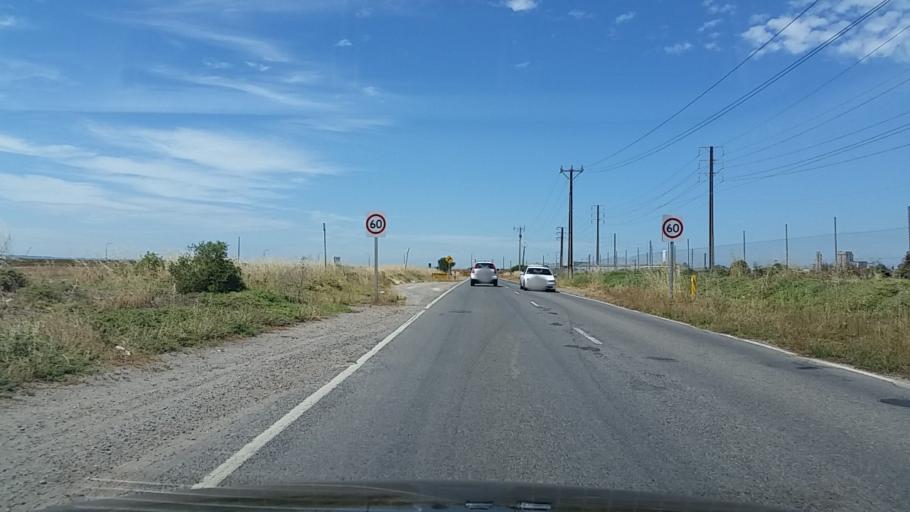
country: AU
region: South Australia
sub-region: Port Adelaide Enfield
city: Birkenhead
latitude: -34.8147
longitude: 138.5253
